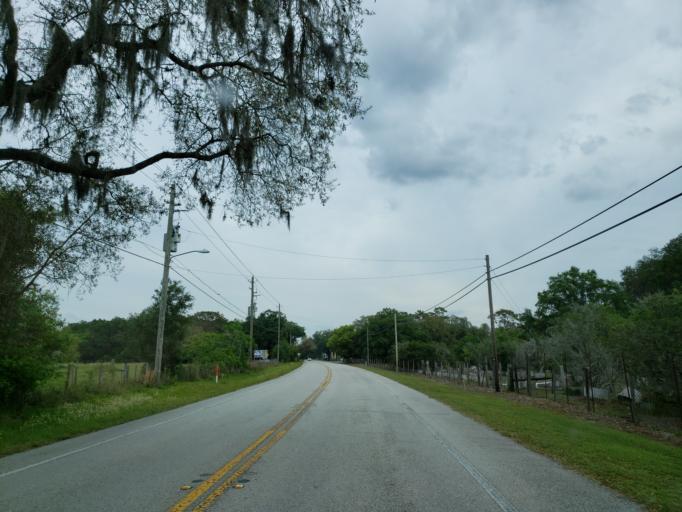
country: US
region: Florida
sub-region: Hillsborough County
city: Keystone
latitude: 28.1396
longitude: -82.6305
